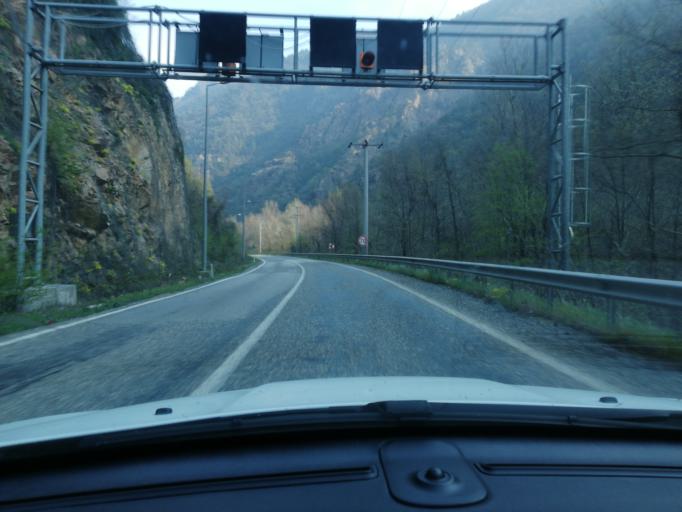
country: TR
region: Karabuk
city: Yenice
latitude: 41.1786
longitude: 32.4477
